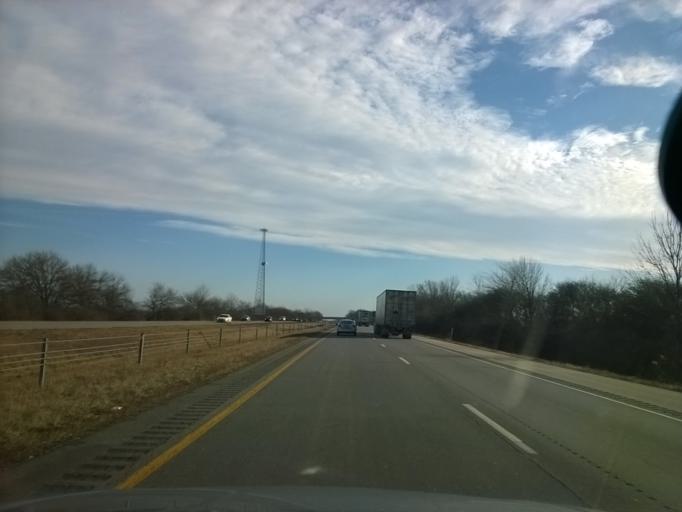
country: US
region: Indiana
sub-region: Johnson County
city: Franklin
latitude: 39.4598
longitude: -86.0018
